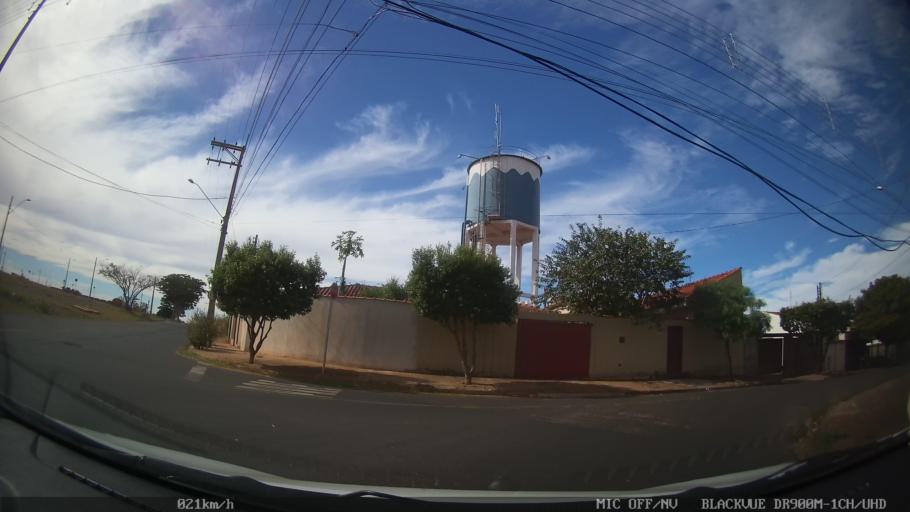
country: BR
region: Sao Paulo
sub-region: Catanduva
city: Catanduva
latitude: -21.1213
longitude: -48.9390
